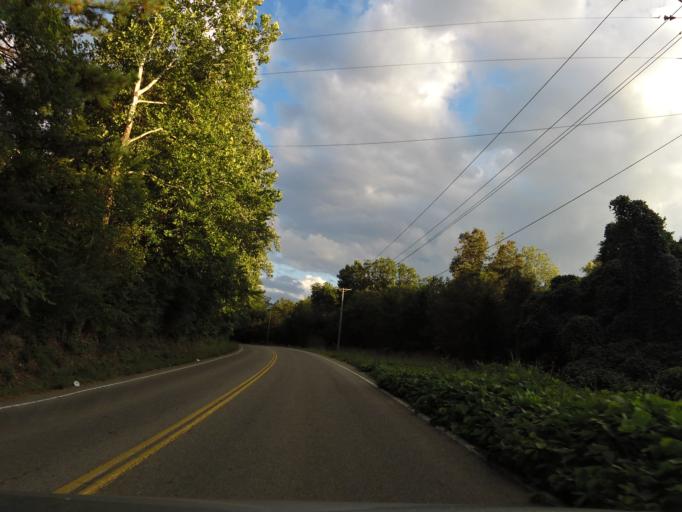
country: US
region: Tennessee
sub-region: Jefferson County
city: Jefferson City
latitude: 36.1473
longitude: -83.5283
